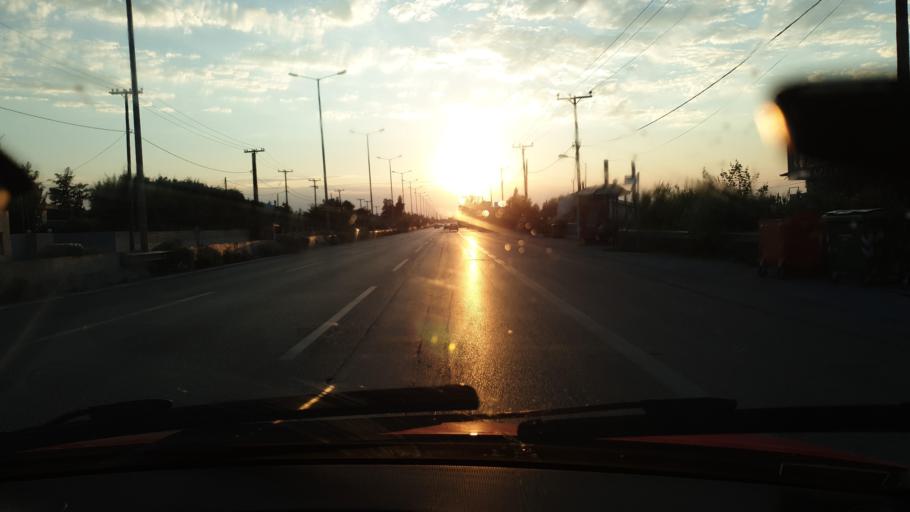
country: GR
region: Central Macedonia
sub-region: Nomos Thessalonikis
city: Plagiari
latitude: 40.5002
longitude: 22.9602
